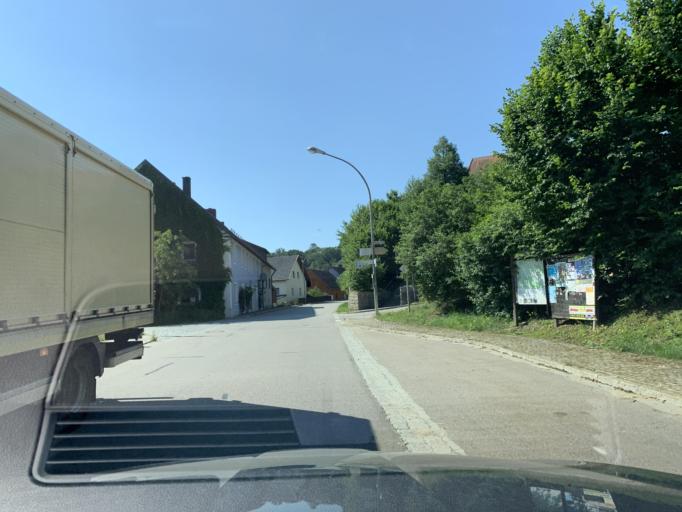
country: DE
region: Bavaria
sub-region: Upper Palatinate
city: Pettendorf
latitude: 49.3523
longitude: 12.3626
